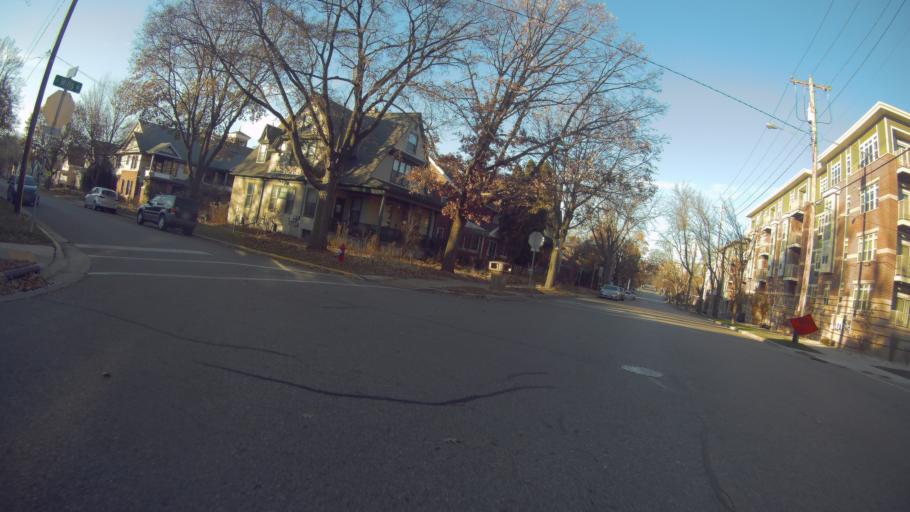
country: US
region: Wisconsin
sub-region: Dane County
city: Madison
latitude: 43.0652
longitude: -89.4042
